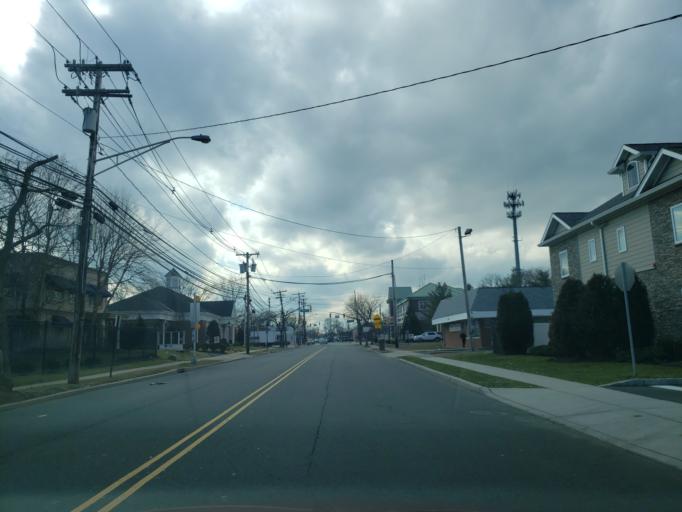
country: US
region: New Jersey
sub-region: Union County
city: Springfield
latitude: 40.7067
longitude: -74.3155
